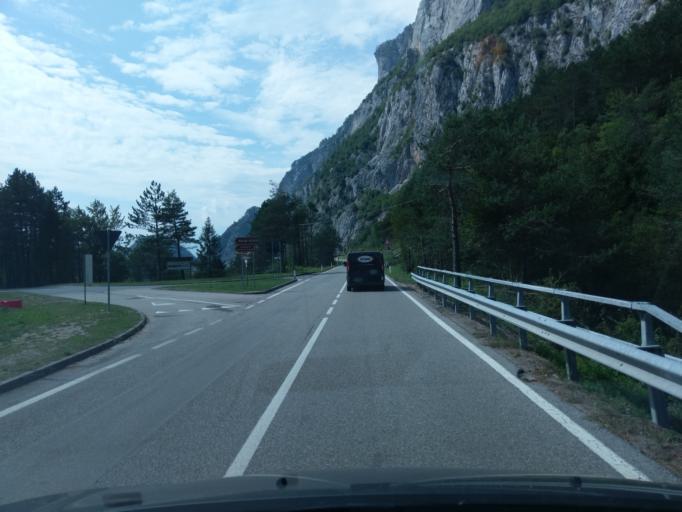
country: IT
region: Trentino-Alto Adige
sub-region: Provincia di Trento
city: San Lorenzo in Banale
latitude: 46.0959
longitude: 10.9319
